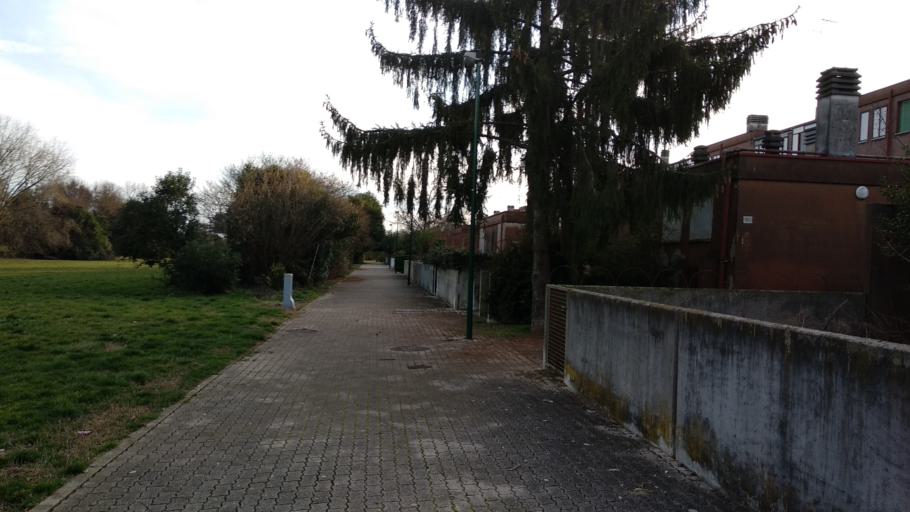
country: IT
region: Veneto
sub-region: Provincia di Venezia
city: Campalto
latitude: 45.4844
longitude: 12.2690
